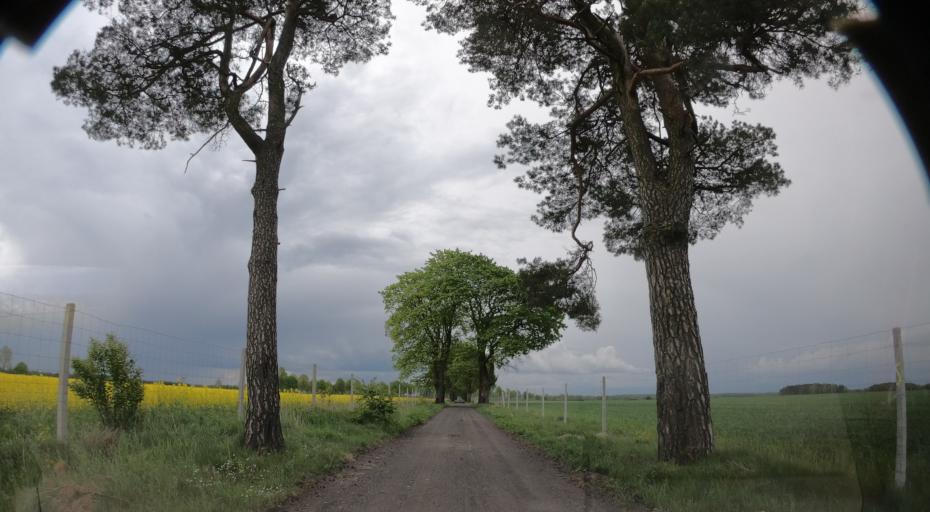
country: PL
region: West Pomeranian Voivodeship
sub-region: Powiat koszalinski
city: Bobolice
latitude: 54.0518
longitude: 16.4230
